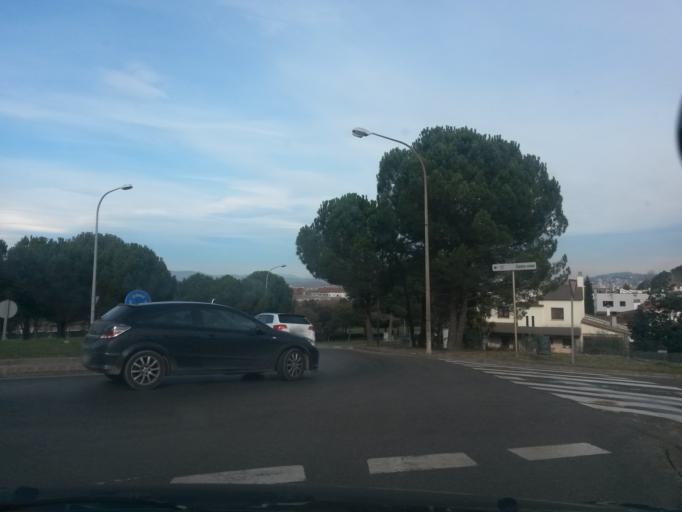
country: ES
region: Catalonia
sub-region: Provincia de Girona
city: Salt
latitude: 41.9598
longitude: 2.8138
